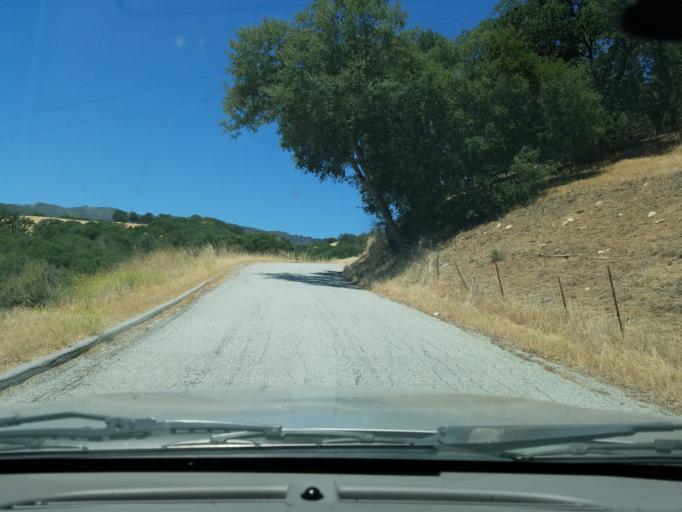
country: US
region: California
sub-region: Monterey County
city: Gonzales
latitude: 36.3403
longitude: -121.5035
